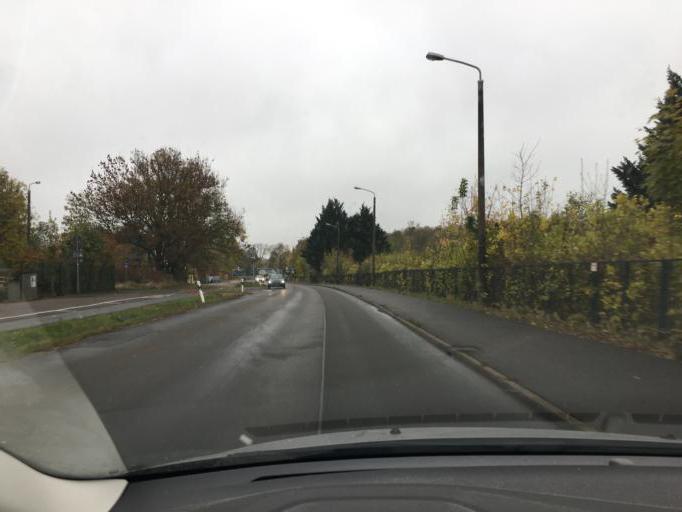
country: DE
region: Saxony
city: Leipzig
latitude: 51.3315
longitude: 12.4269
